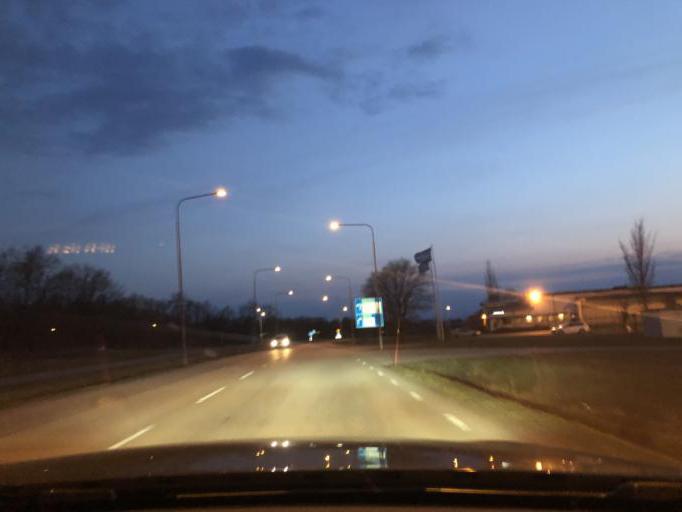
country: SE
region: Kalmar
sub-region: Kalmar Kommun
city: Kalmar
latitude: 56.6815
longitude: 16.3175
